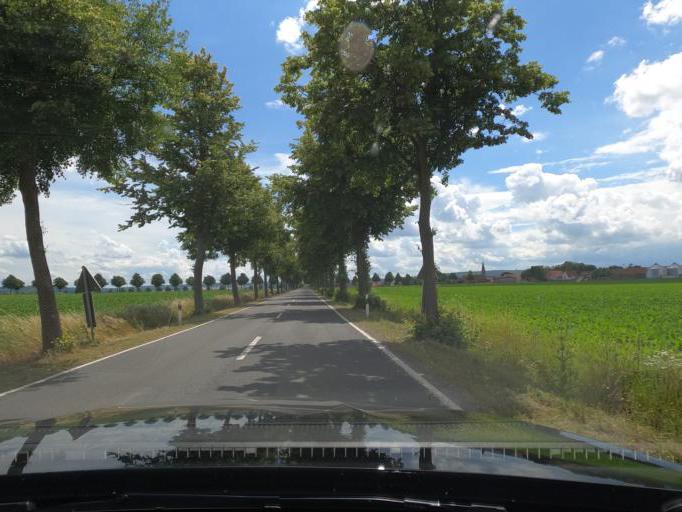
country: DE
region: Lower Saxony
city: Schellerten
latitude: 52.1769
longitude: 10.0421
